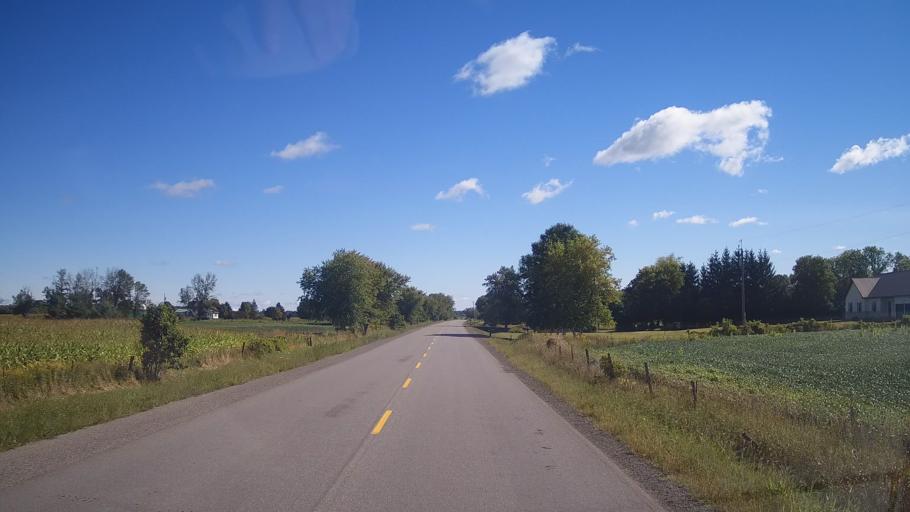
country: CA
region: Ontario
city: Prescott
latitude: 44.8999
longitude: -75.4526
